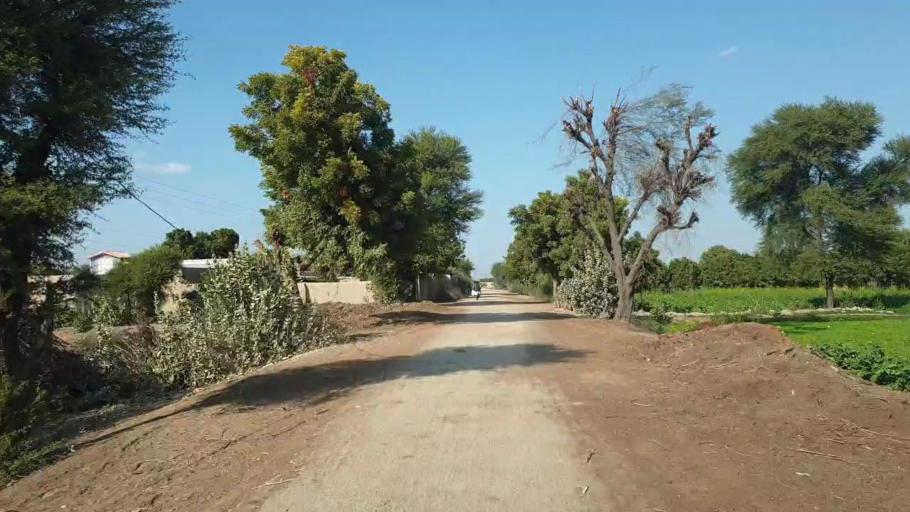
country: PK
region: Sindh
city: Shahpur Chakar
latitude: 26.1036
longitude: 68.5927
